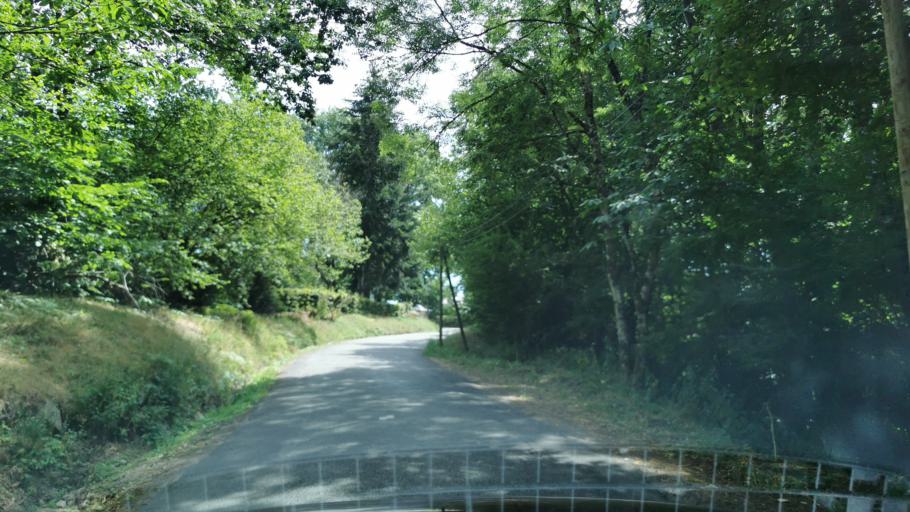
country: FR
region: Bourgogne
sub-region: Departement de Saone-et-Loire
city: Etang-sur-Arroux
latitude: 46.8086
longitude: 4.2600
